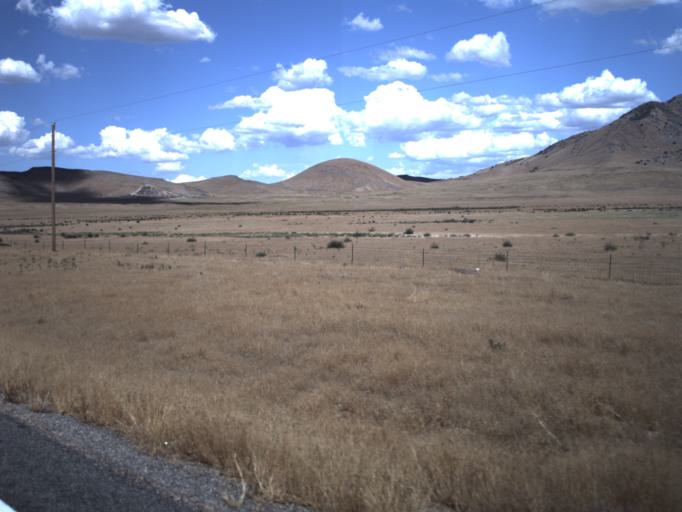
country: US
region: Utah
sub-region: Millard County
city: Delta
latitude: 39.6333
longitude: -112.3082
